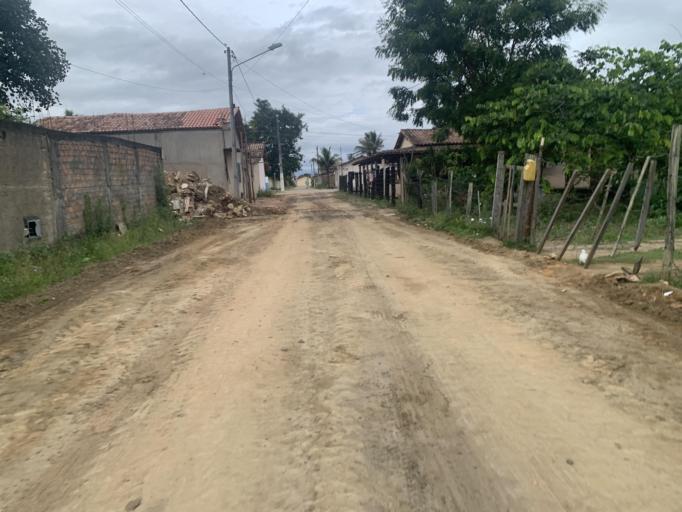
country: BR
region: Bahia
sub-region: Medeiros Neto
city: Medeiros Neto
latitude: -17.3921
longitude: -40.2308
